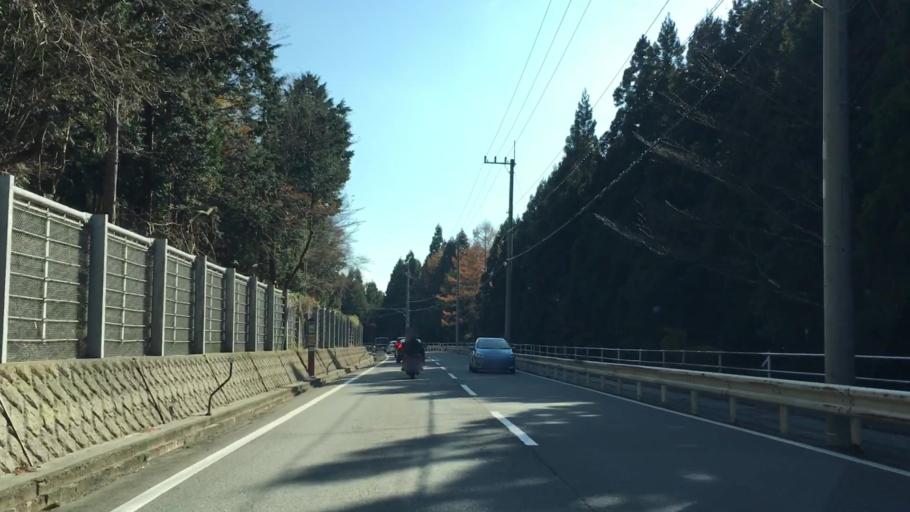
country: JP
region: Shizuoka
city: Gotemba
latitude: 35.3763
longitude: 138.8584
